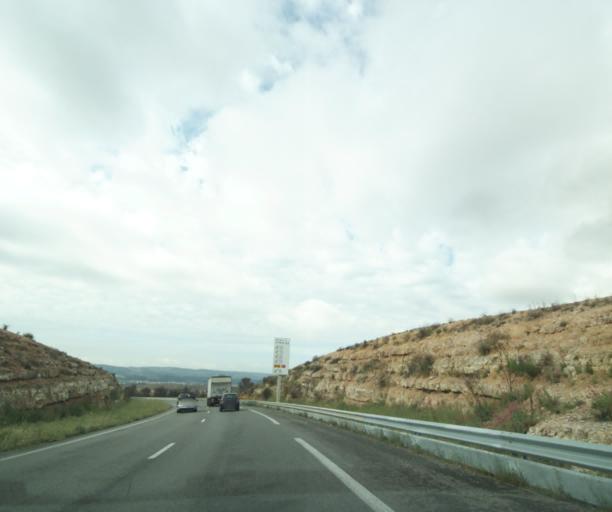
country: FR
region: Provence-Alpes-Cote d'Azur
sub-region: Departement des Bouches-du-Rhone
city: Les Pennes-Mirabeau
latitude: 43.4502
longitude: 5.2981
